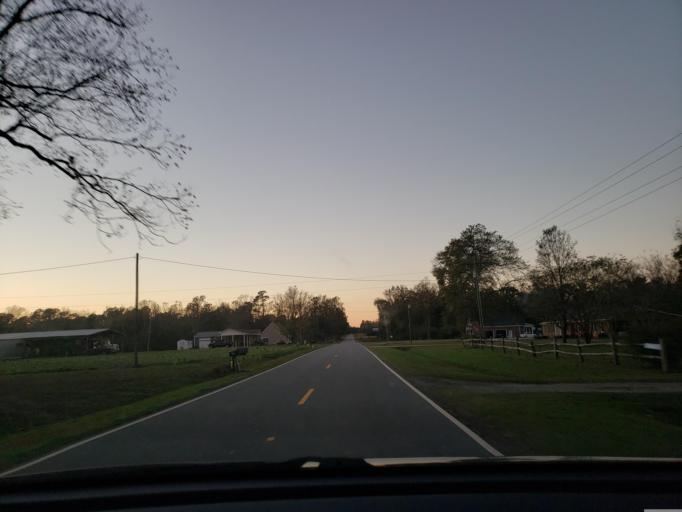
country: US
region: North Carolina
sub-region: Duplin County
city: Beulaville
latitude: 34.7706
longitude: -77.7399
